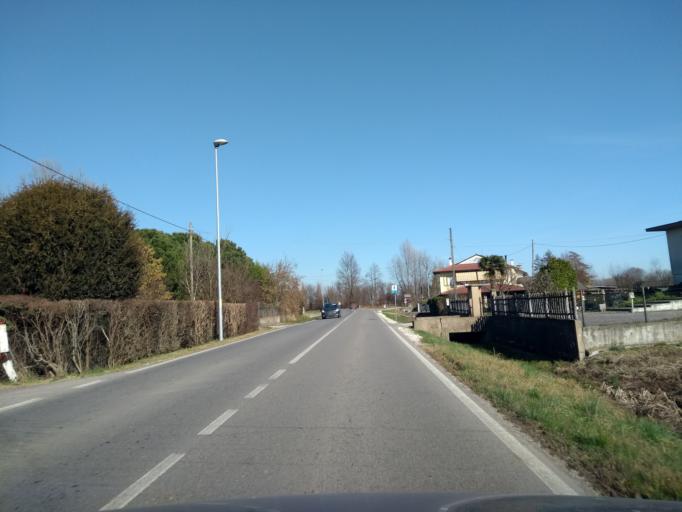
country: IT
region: Veneto
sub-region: Provincia di Vicenza
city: Bolzano Vicentino
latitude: 45.5987
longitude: 11.6405
